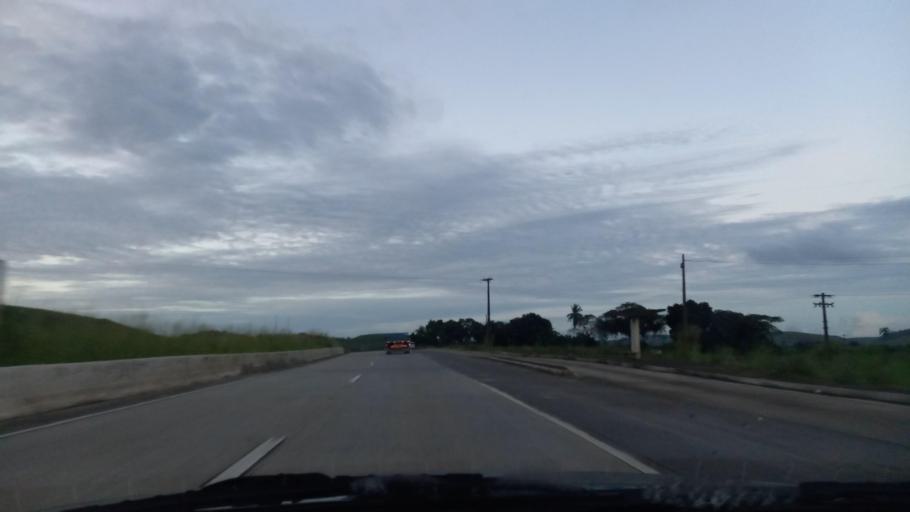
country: BR
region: Pernambuco
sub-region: Ribeirao
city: Ribeirao
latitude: -8.5338
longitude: -35.3907
